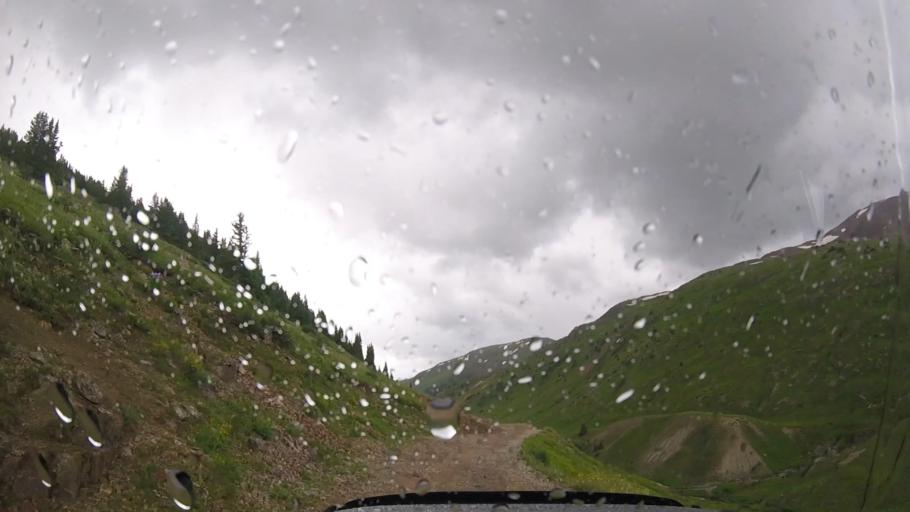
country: US
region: Colorado
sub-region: Ouray County
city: Ouray
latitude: 37.9466
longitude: -107.5741
